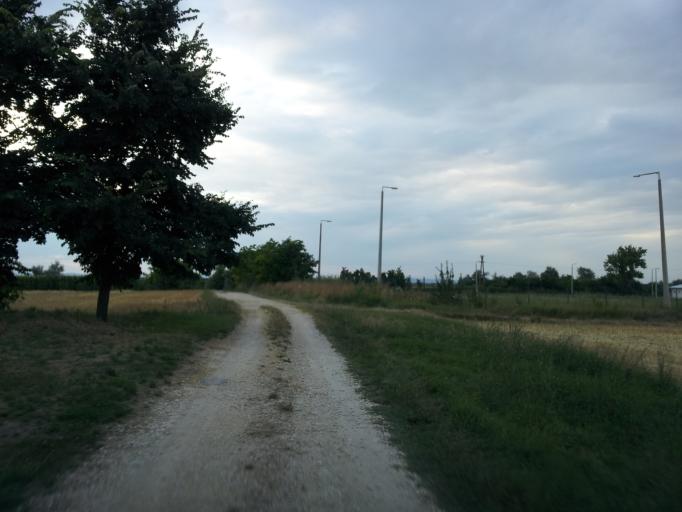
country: HU
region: Somogy
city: Adand
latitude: 46.8861
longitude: 18.1630
